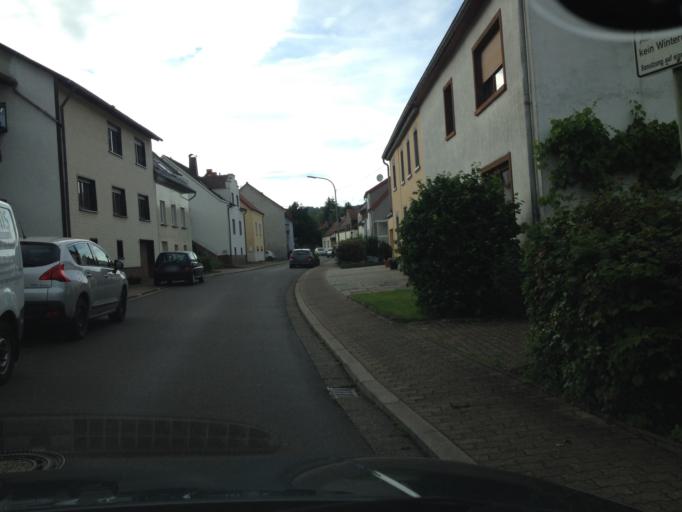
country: DE
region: Saarland
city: Marpingen
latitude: 49.4742
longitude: 7.0629
